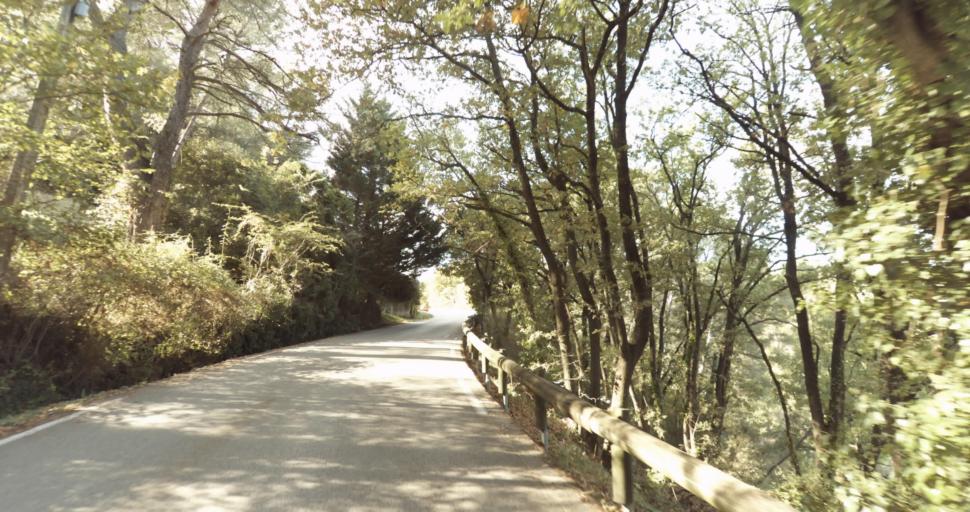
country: FR
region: Provence-Alpes-Cote d'Azur
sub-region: Departement des Bouches-du-Rhone
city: Venelles
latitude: 43.6023
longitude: 5.4820
